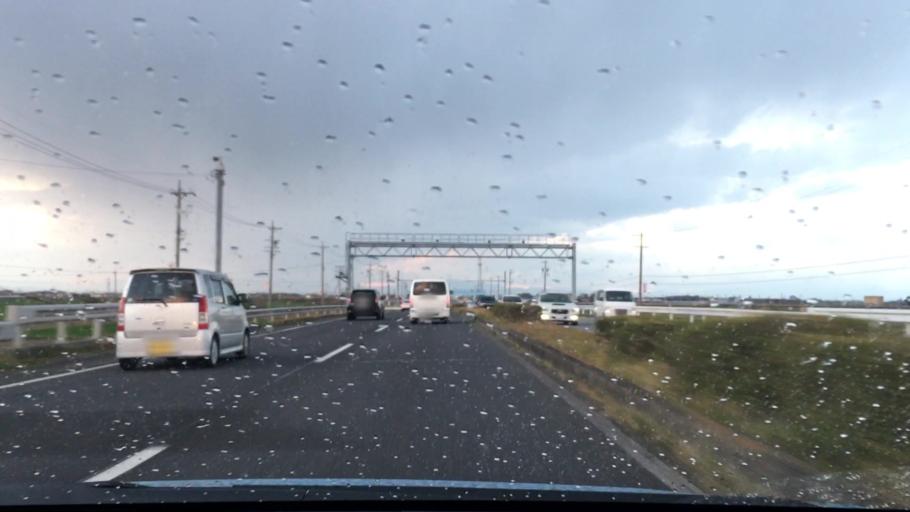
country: JP
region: Mie
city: Ise
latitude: 34.5585
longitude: 136.6473
